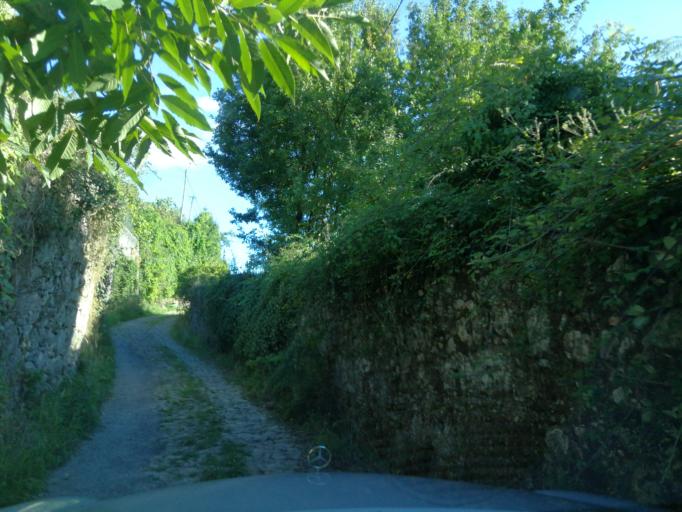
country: PT
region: Braga
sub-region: Braga
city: Braga
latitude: 41.5478
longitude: -8.3944
